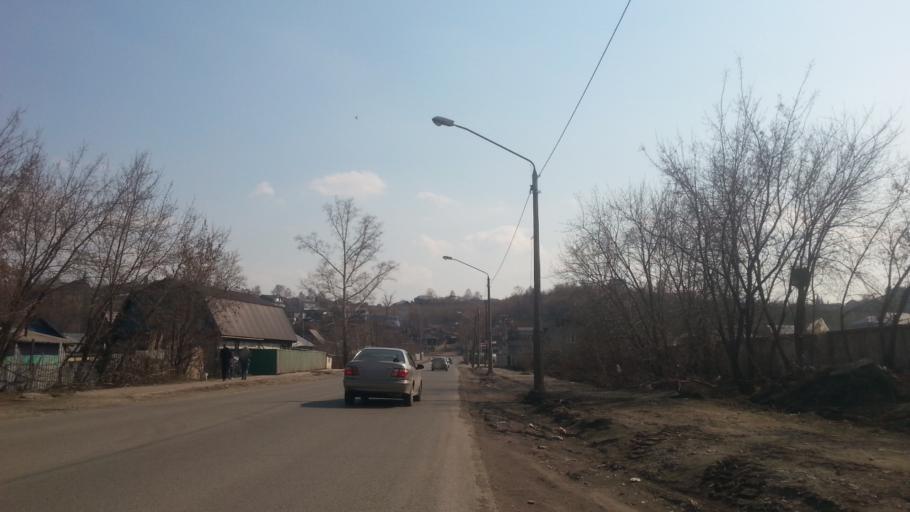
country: RU
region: Altai Krai
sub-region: Gorod Barnaulskiy
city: Barnaul
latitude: 53.3213
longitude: 83.7694
